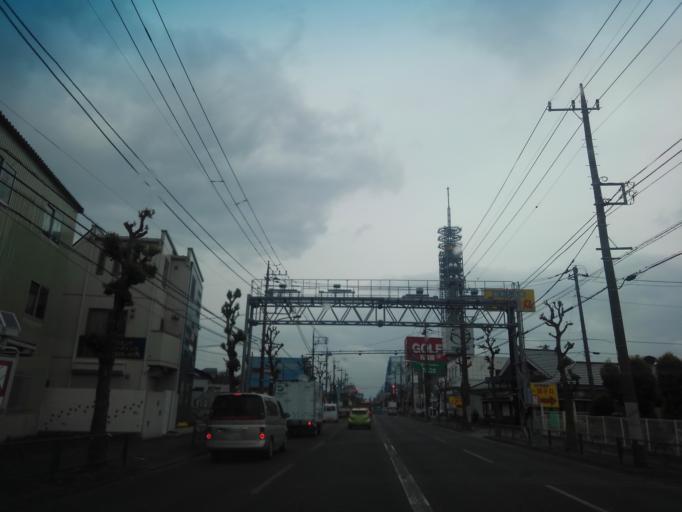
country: JP
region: Tokyo
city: Tanashicho
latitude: 35.7369
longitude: 139.5188
